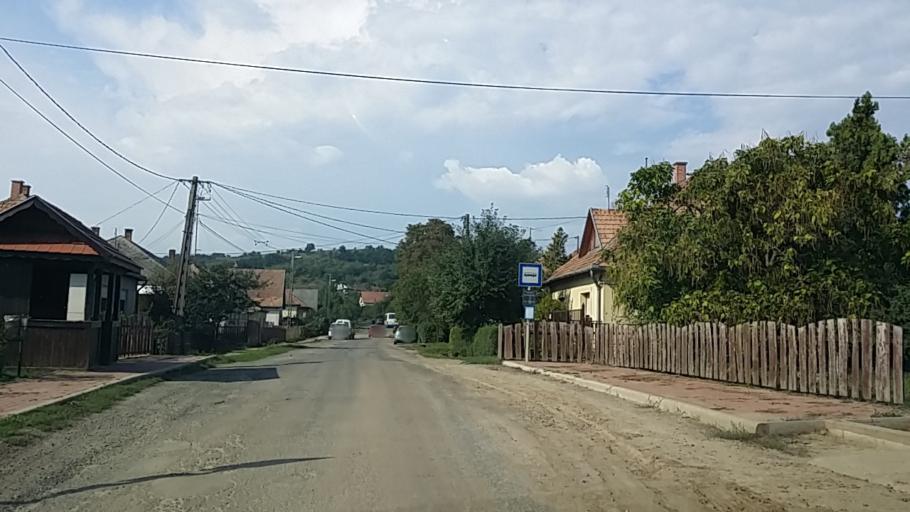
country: HU
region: Nograd
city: Bujak
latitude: 47.8602
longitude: 19.5110
